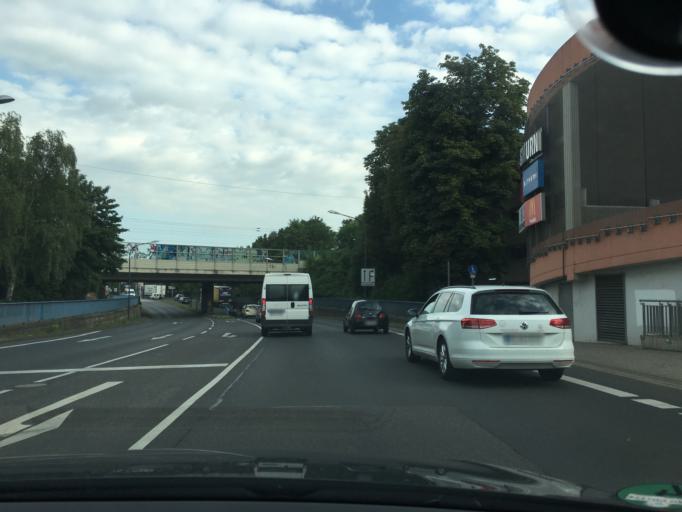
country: DE
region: North Rhine-Westphalia
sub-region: Regierungsbezirk Koln
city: Dueren
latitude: 50.8055
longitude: 6.4793
